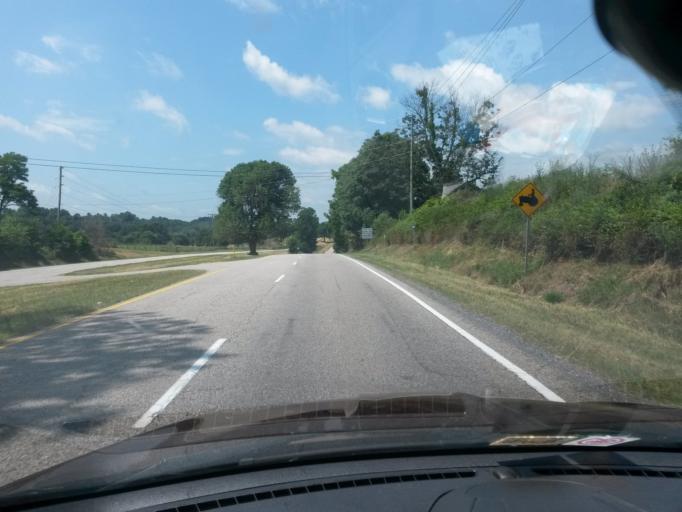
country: US
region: Virginia
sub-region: City of Buena Vista
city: Buena Vista
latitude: 37.8759
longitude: -79.2972
